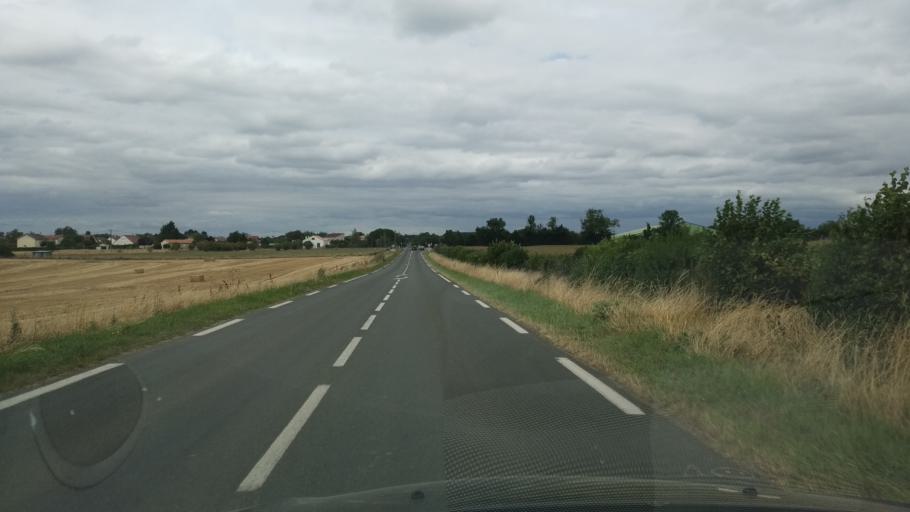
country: FR
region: Poitou-Charentes
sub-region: Departement de la Vienne
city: Roches-Premarie-Andille
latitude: 46.4739
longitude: 0.3688
